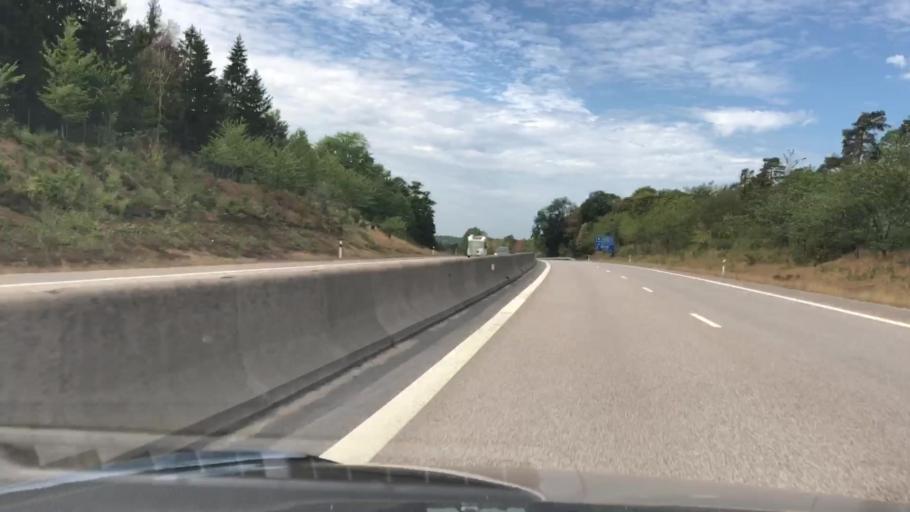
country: SE
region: Blekinge
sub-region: Karlskrona Kommun
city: Nattraby
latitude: 56.2101
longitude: 15.5534
